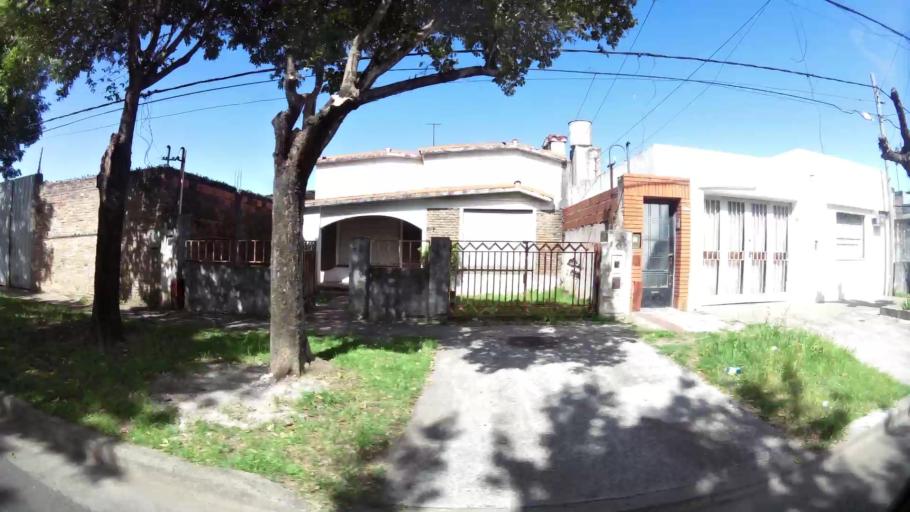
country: AR
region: Santa Fe
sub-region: Departamento de Rosario
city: Rosario
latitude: -32.9365
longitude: -60.7163
